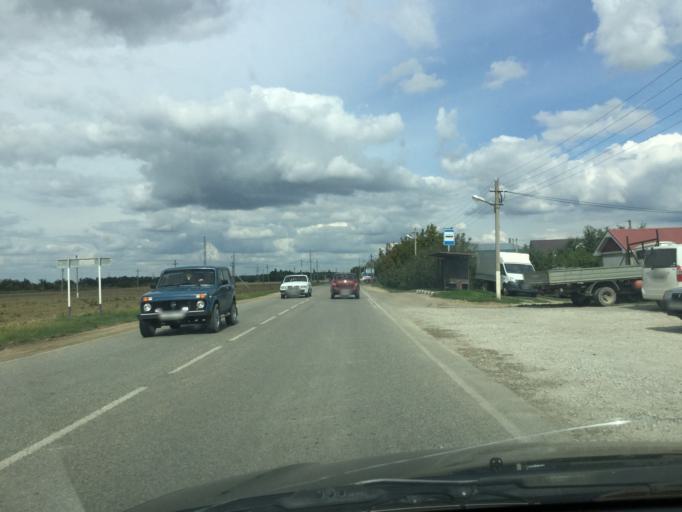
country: RU
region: Krasnodarskiy
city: Sovkhoznyy
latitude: 45.2761
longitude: 38.0949
